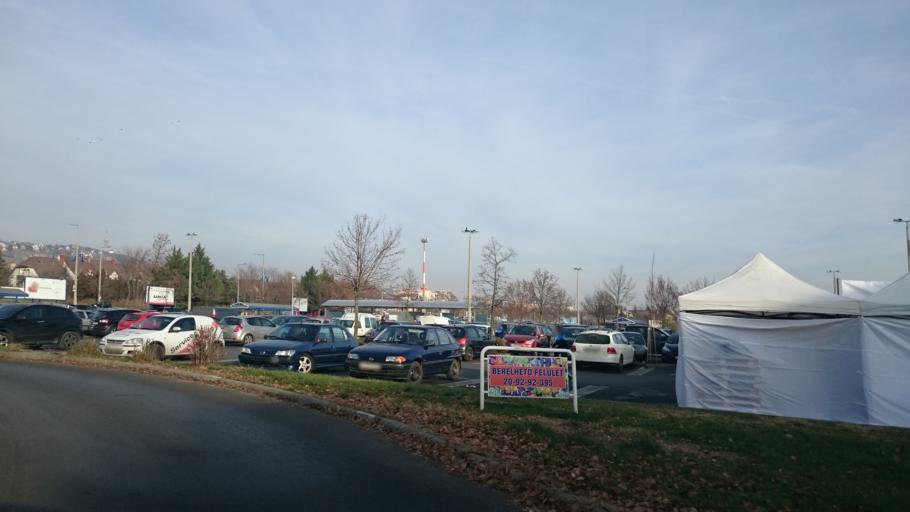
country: HU
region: Baranya
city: Pellerd
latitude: 46.0639
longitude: 18.1832
